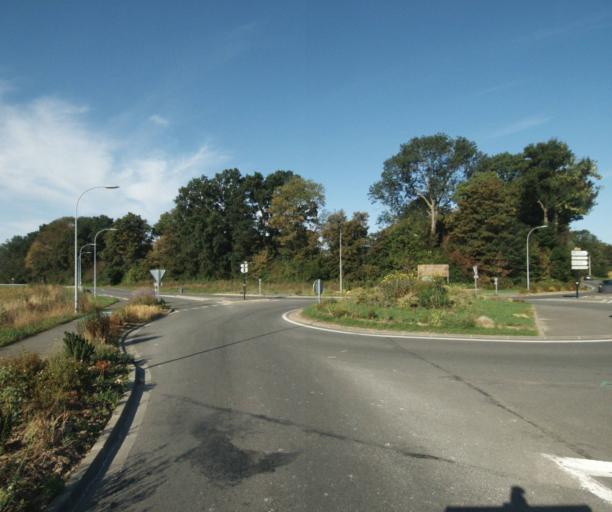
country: FR
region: Nord-Pas-de-Calais
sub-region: Departement du Nord
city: Cysoing
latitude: 50.5767
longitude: 3.1944
